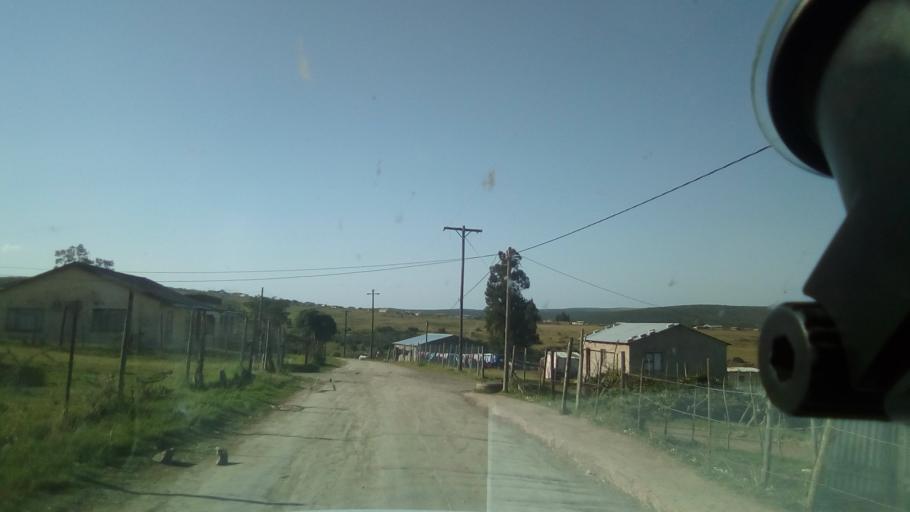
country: ZA
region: Eastern Cape
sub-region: Buffalo City Metropolitan Municipality
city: Bhisho
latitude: -32.8116
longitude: 27.3573
